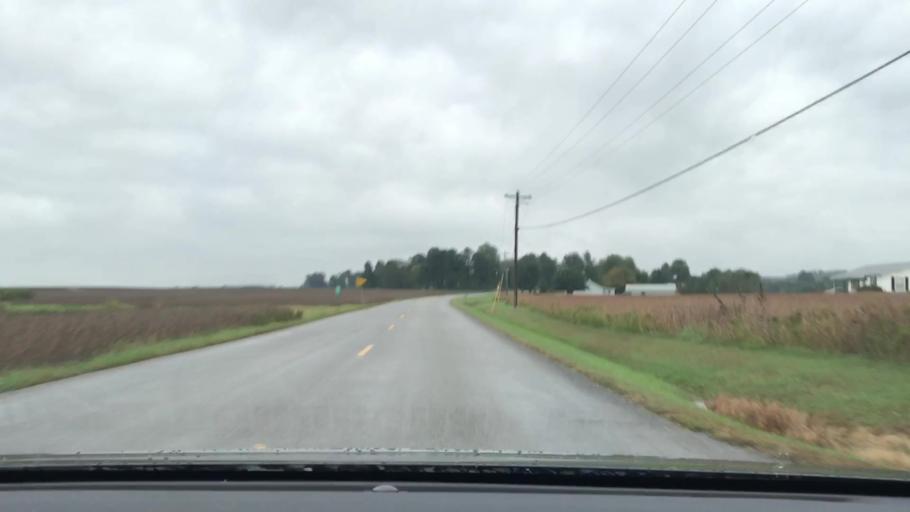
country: US
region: Kentucky
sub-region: McLean County
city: Calhoun
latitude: 37.4360
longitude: -87.2479
